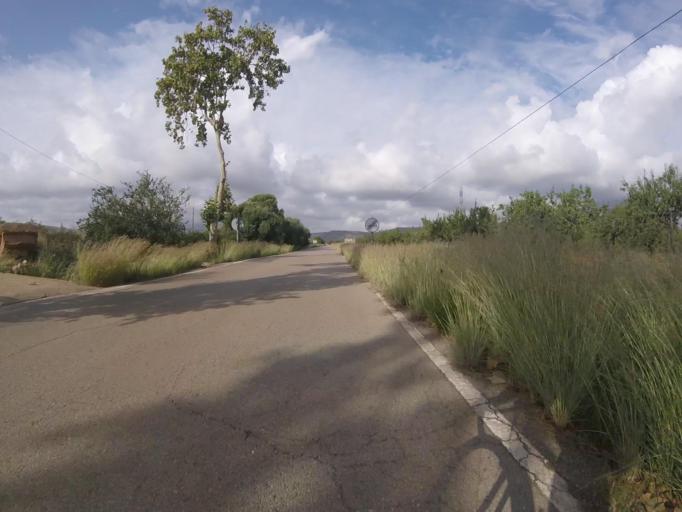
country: ES
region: Valencia
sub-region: Provincia de Castello
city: Orpesa/Oropesa del Mar
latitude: 40.1390
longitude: 0.1502
